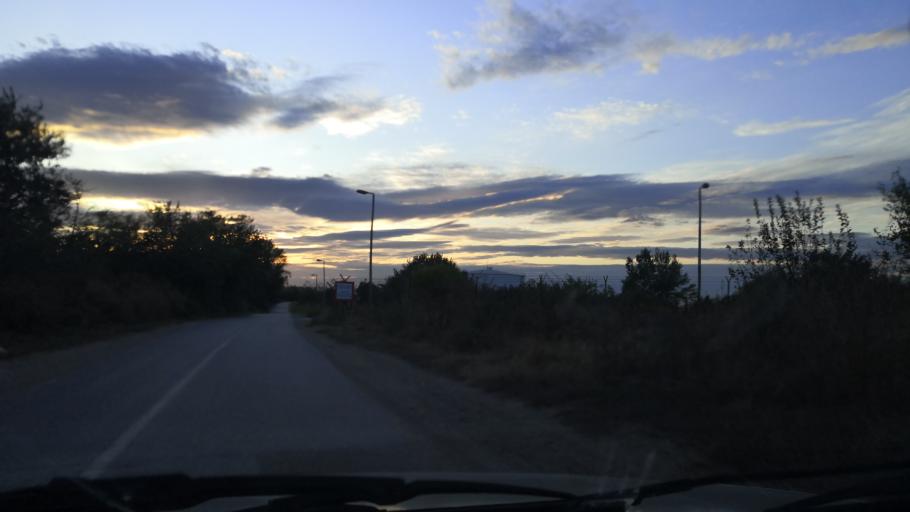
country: RO
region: Mehedinti
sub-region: Comuna Gruia
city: Izvoarele
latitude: 44.2863
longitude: 22.6317
